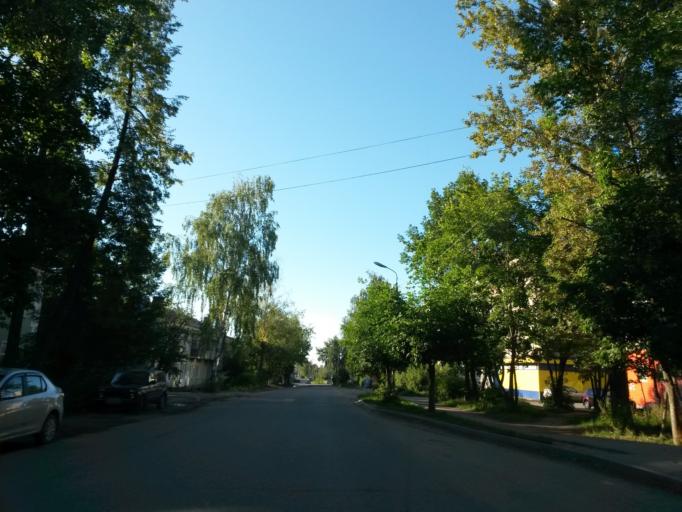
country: RU
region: Jaroslavl
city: Gavrilov-Yam
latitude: 57.3045
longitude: 39.8618
